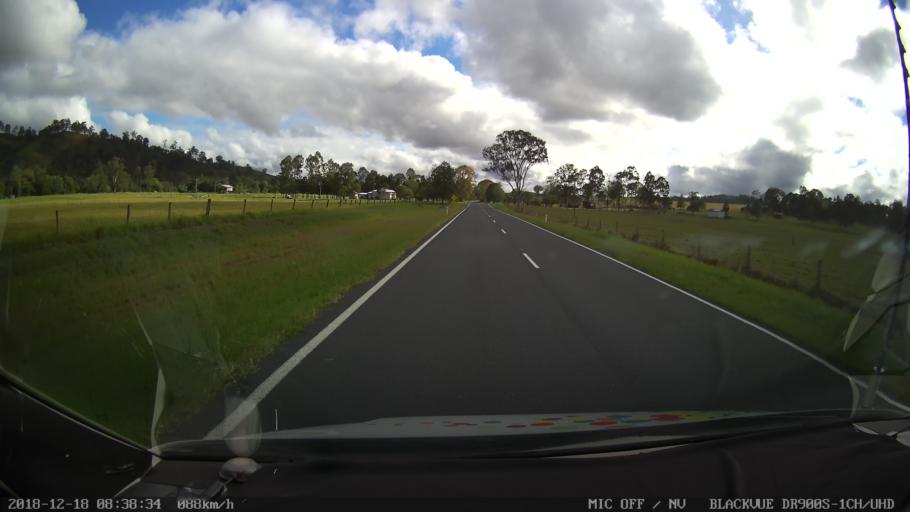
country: AU
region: New South Wales
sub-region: Kyogle
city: Kyogle
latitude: -28.2550
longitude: 152.8291
